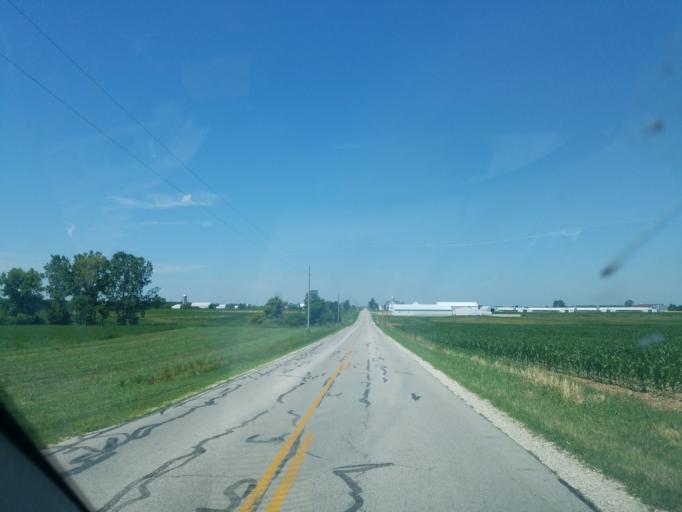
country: US
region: Ohio
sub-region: Mercer County
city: Saint Henry
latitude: 40.4506
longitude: -84.7010
